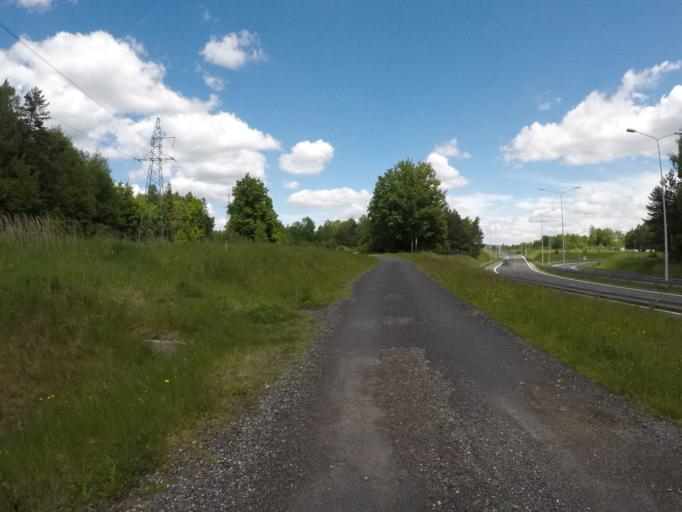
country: PL
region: Swietokrzyskie
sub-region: Powiat kielecki
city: Zagnansk
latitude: 50.9403
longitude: 20.6704
